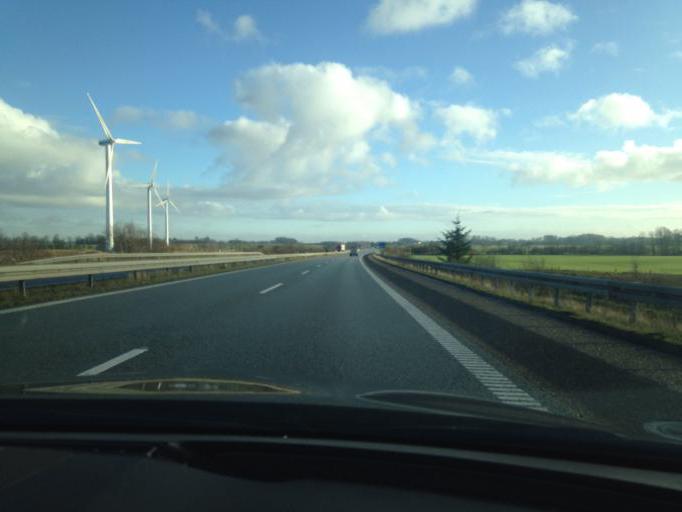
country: DK
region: South Denmark
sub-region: Vejen Kommune
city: Brorup
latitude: 55.5088
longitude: 8.9937
